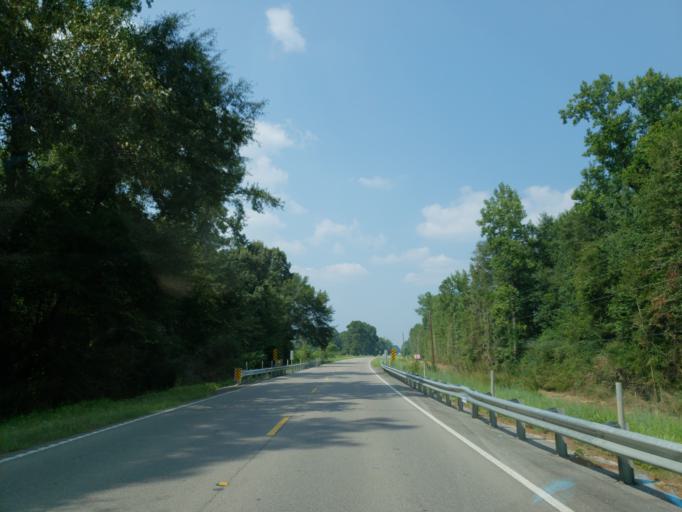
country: US
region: Mississippi
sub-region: Forrest County
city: Glendale
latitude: 31.4452
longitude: -89.2865
